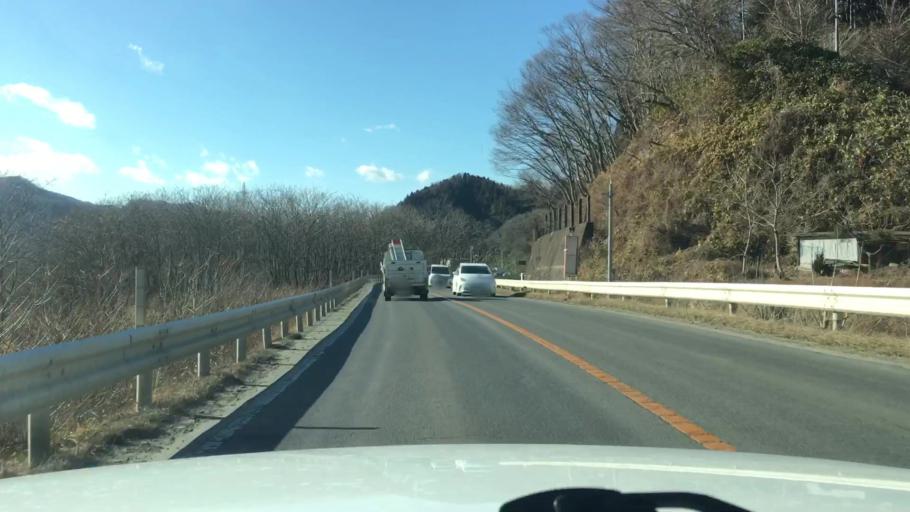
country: JP
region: Iwate
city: Miyako
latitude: 39.6325
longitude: 141.8860
